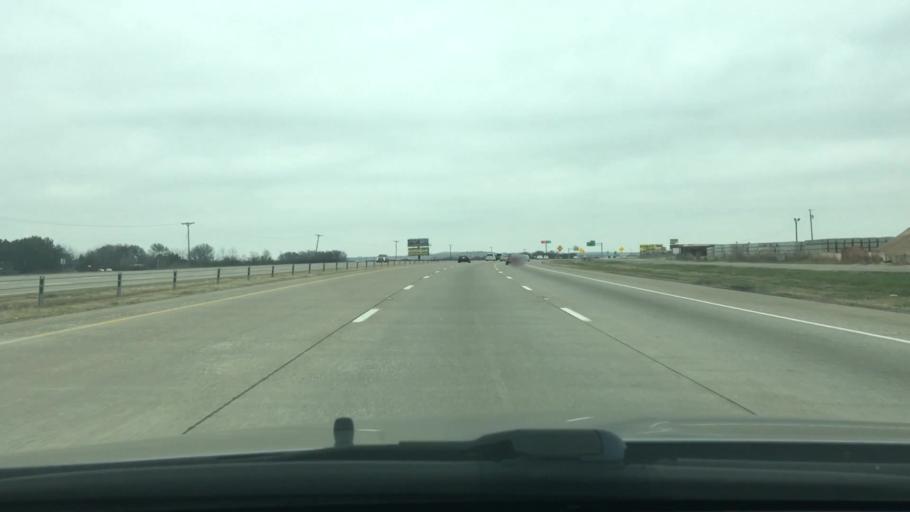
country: US
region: Texas
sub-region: Ellis County
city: Palmer
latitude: 32.4266
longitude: -96.6584
